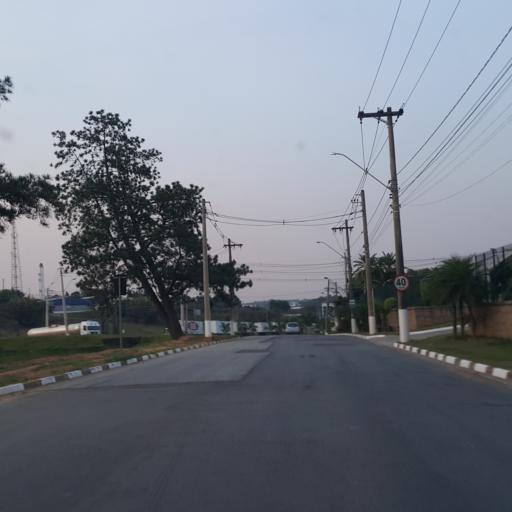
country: BR
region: Sao Paulo
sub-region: Vinhedo
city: Vinhedo
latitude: -23.0694
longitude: -47.0016
